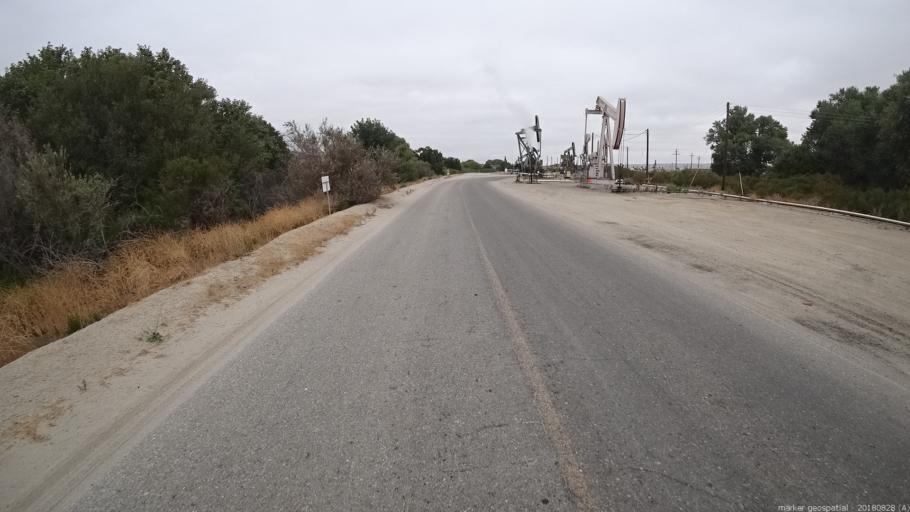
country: US
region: California
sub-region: San Luis Obispo County
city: Lake Nacimiento
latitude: 35.9591
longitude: -120.8788
